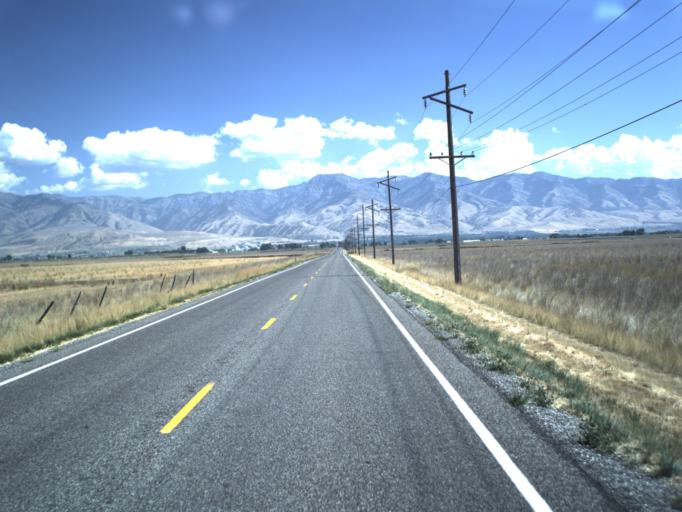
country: US
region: Utah
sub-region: Cache County
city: Benson
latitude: 41.8449
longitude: -111.9413
